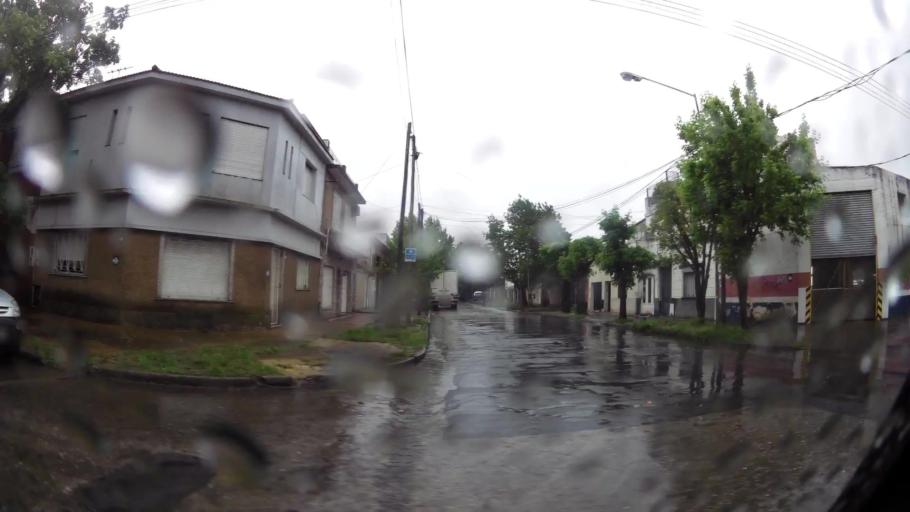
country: AR
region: Buenos Aires
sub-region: Partido de Lanus
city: Lanus
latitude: -34.7170
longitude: -58.3994
